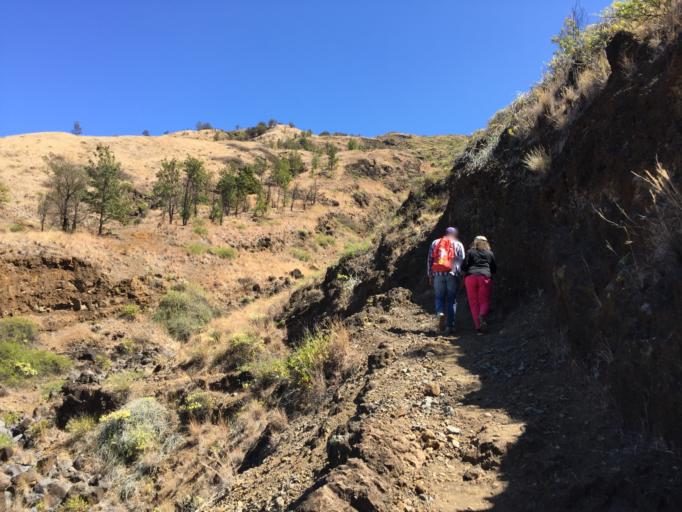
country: CV
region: Mosteiros
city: Porto dos Mosteiros
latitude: 15.0065
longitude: -24.3721
